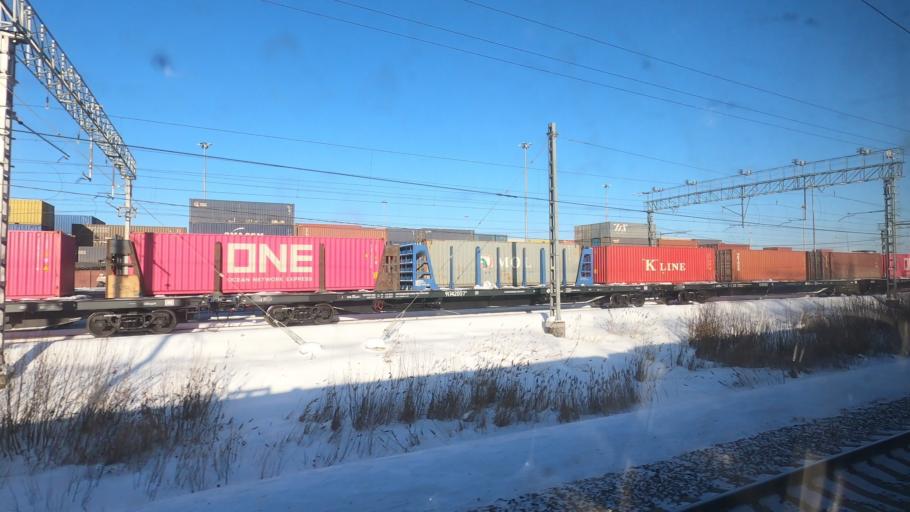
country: RU
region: Moskovskaya
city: Elektrougli
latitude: 55.7233
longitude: 38.2401
